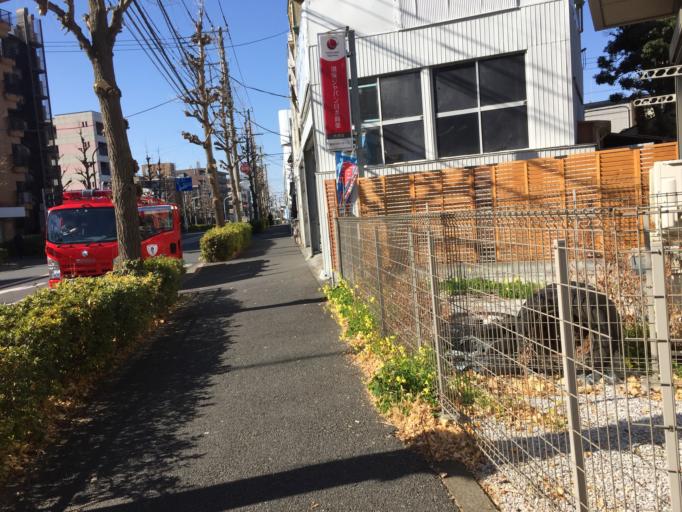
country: JP
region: Tokyo
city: Chofugaoka
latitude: 35.6329
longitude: 139.5874
